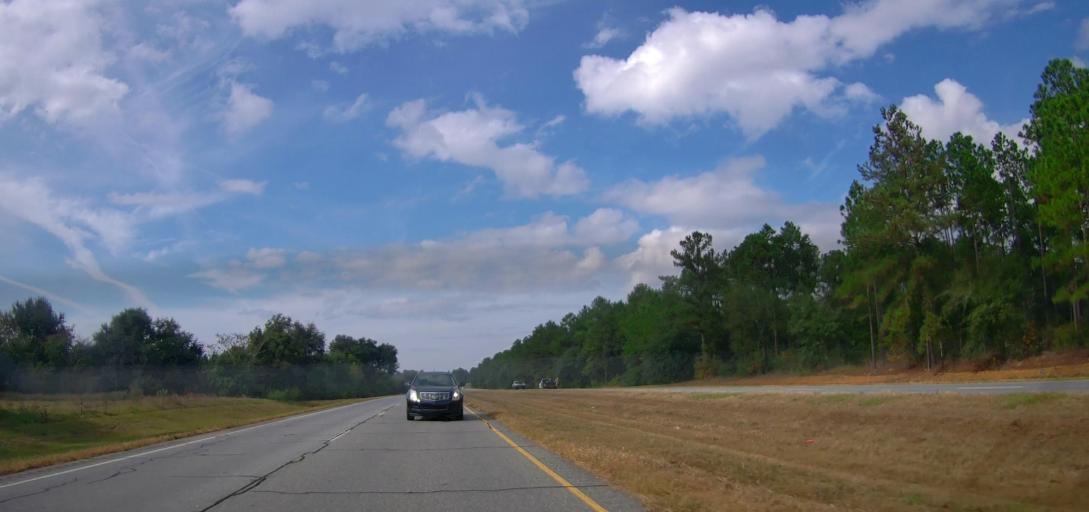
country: US
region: Georgia
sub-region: Mitchell County
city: Camilla
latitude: 31.1943
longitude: -84.1644
